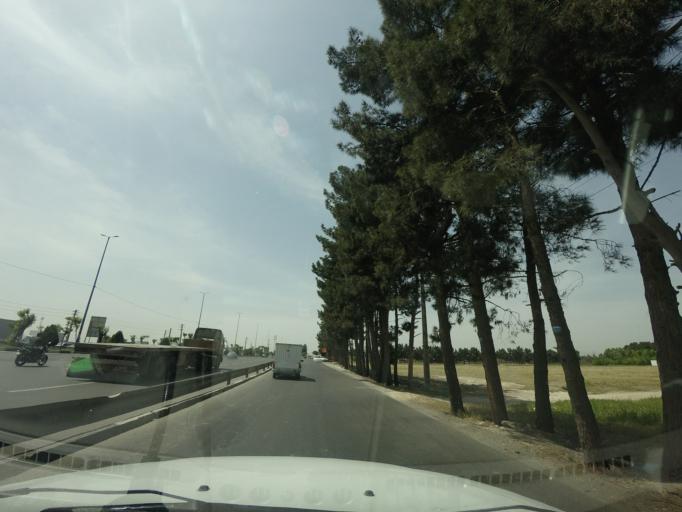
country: IR
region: Tehran
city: Eslamshahr
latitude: 35.5812
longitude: 51.2712
